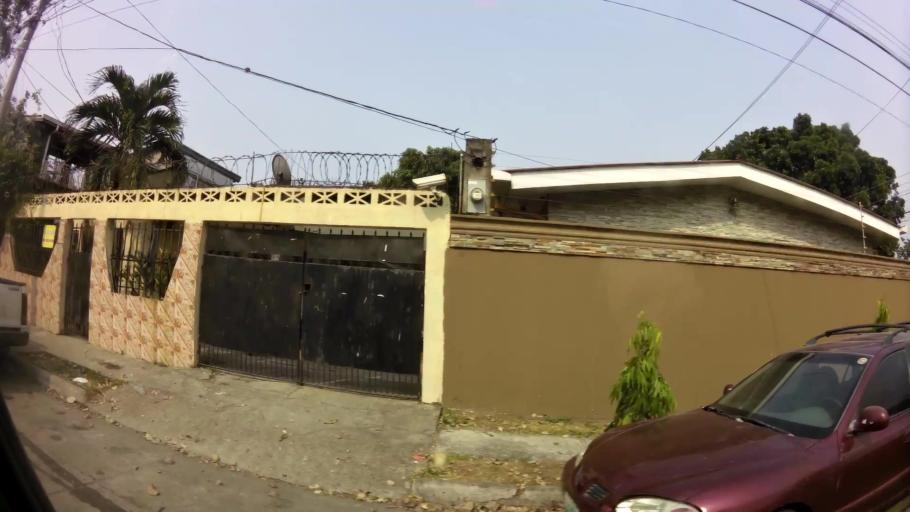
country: HN
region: Cortes
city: Armenta
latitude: 15.4936
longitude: -88.0435
